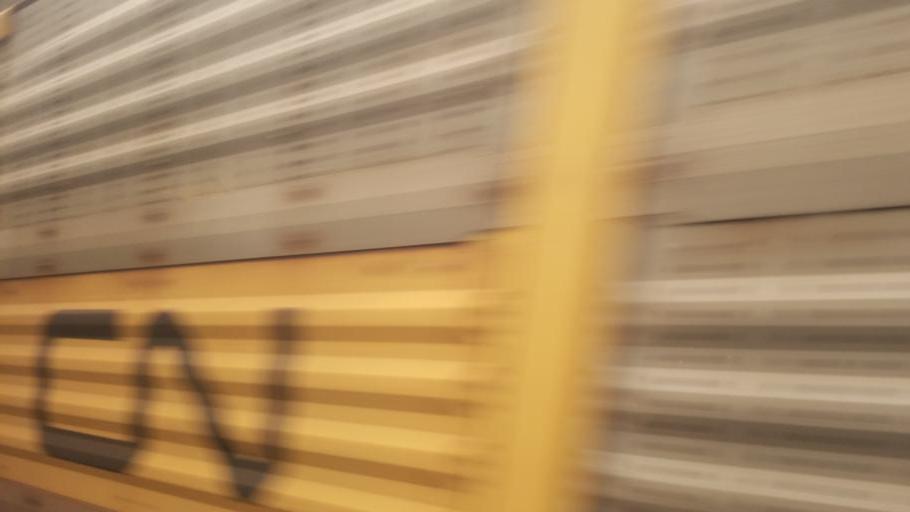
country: US
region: Pennsylvania
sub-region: Somerset County
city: Milford
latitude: 39.8794
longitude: -79.1067
